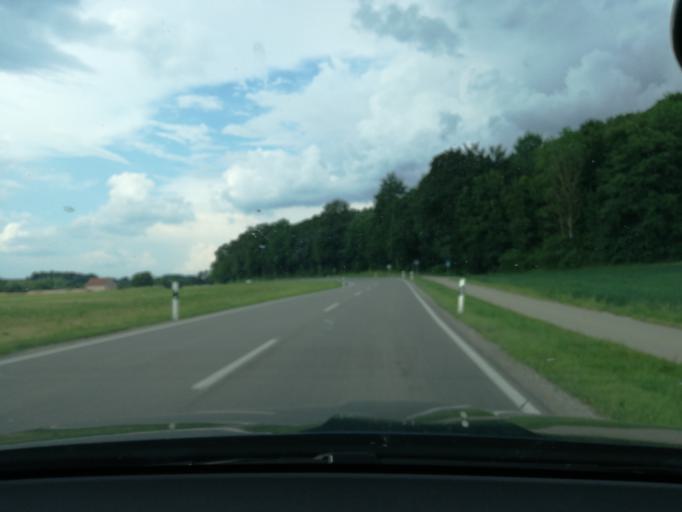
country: DE
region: Bavaria
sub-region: Upper Bavaria
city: Greifenberg
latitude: 48.0641
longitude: 11.0919
